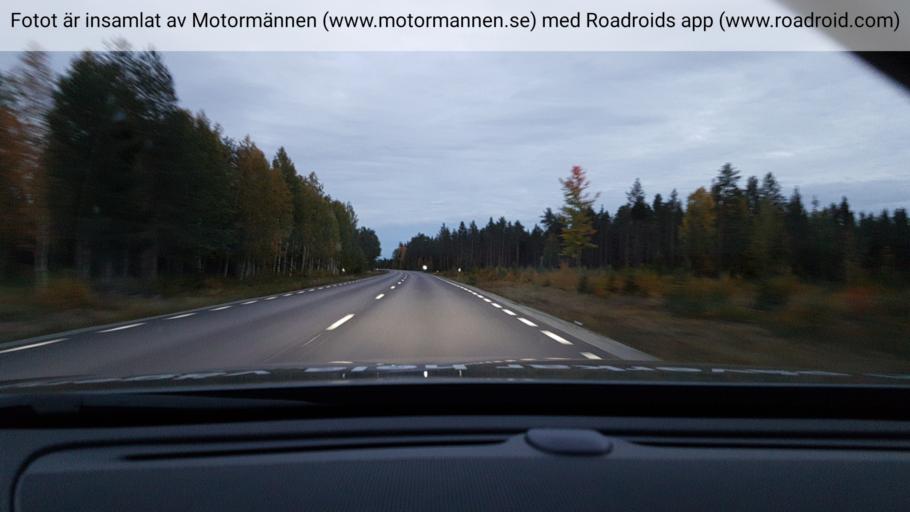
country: SE
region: Norrbotten
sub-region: Alvsbyns Kommun
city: AElvsbyn
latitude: 65.7582
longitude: 20.8854
